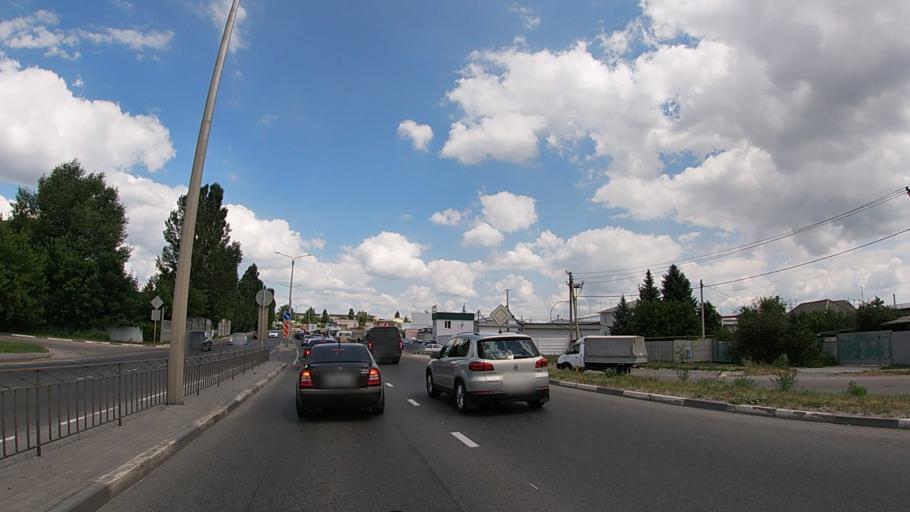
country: RU
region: Belgorod
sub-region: Belgorodskiy Rayon
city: Belgorod
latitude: 50.6096
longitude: 36.5339
